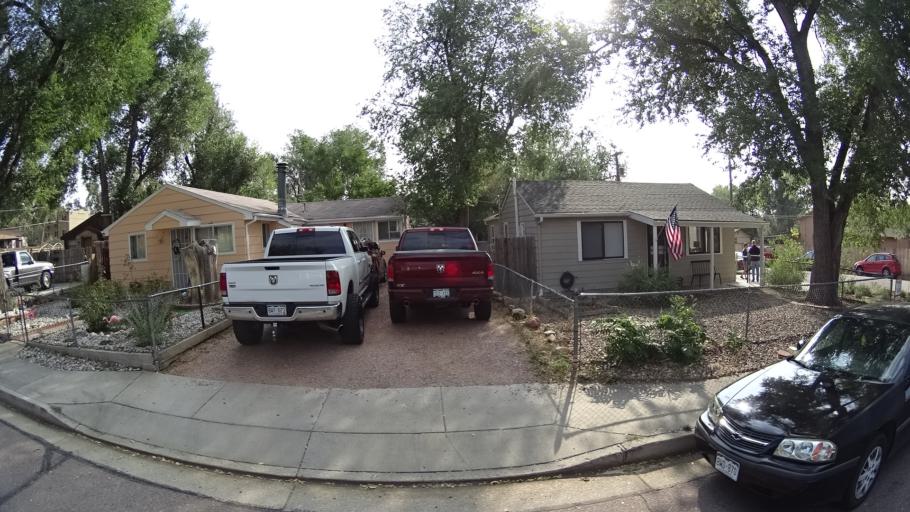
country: US
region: Colorado
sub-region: El Paso County
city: Colorado Springs
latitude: 38.8466
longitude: -104.7804
